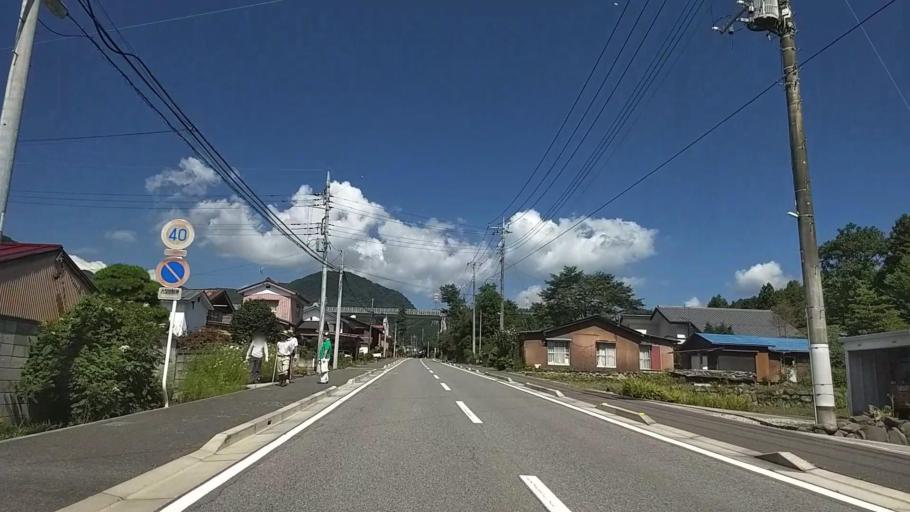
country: JP
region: Gunma
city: Annaka
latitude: 36.3422
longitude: 138.7253
